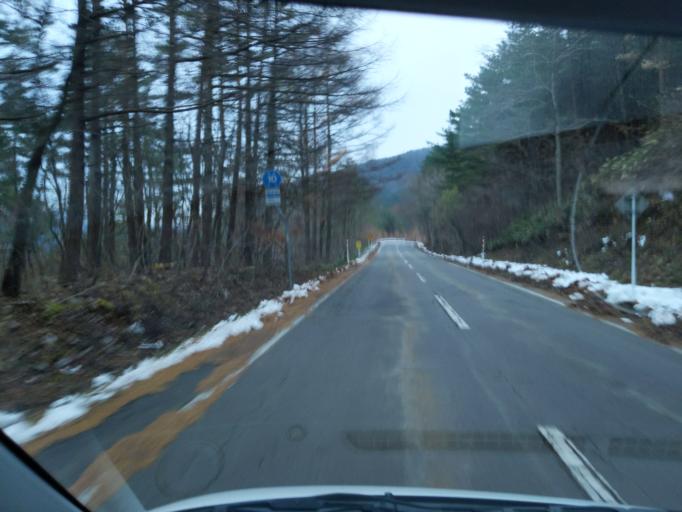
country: JP
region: Iwate
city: Mizusawa
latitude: 39.1490
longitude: 141.3631
